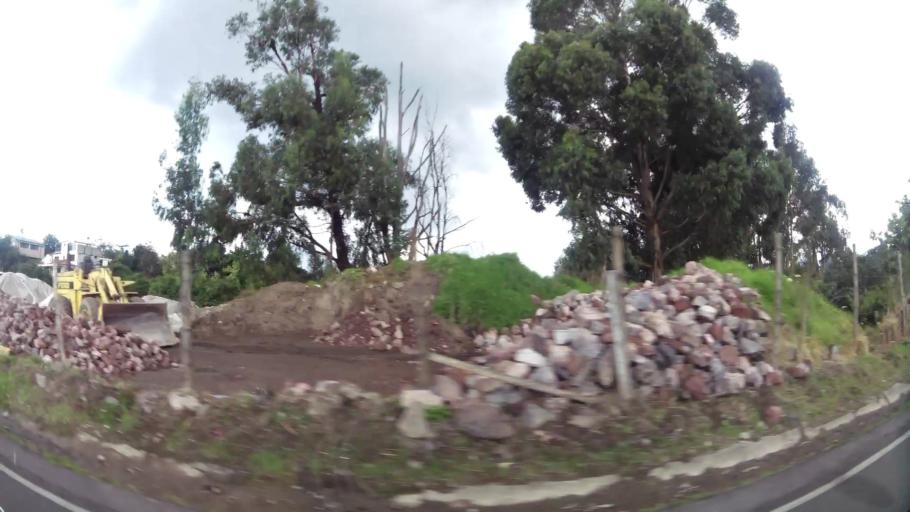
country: EC
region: Pichincha
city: Sangolqui
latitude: -0.3366
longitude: -78.4431
